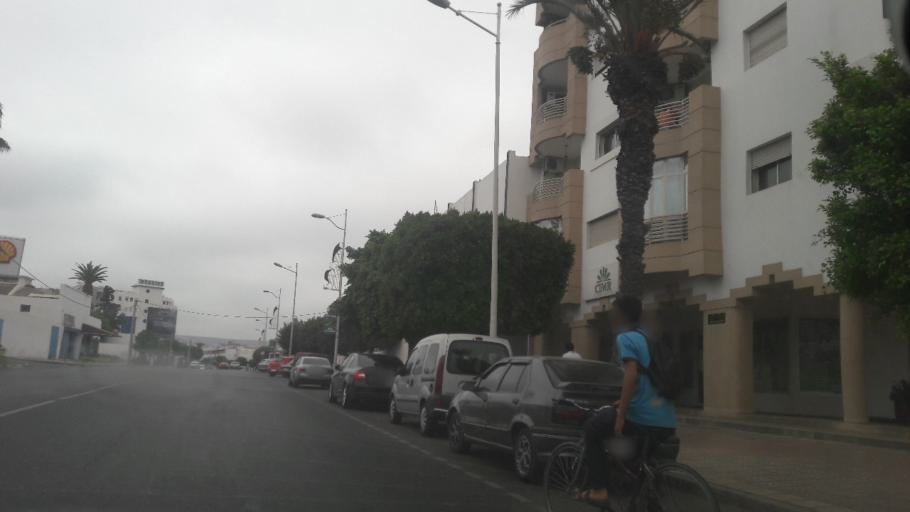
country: MA
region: Souss-Massa-Draa
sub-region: Agadir-Ida-ou-Tnan
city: Agadir
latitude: 30.4081
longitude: -9.5882
